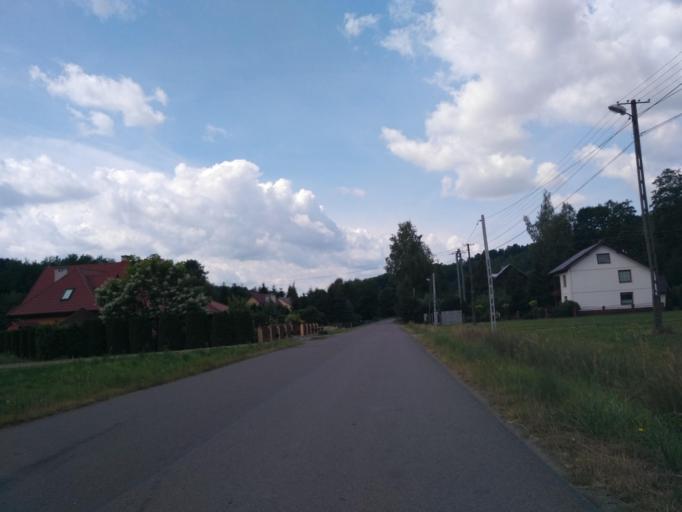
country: PL
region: Subcarpathian Voivodeship
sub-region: Powiat debicki
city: Brzostek
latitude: 49.9187
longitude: 21.3761
